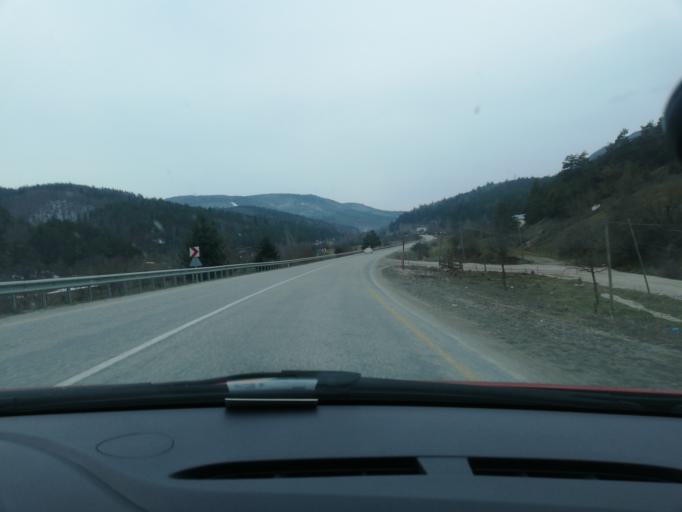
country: TR
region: Kastamonu
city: Kure
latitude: 41.7608
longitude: 33.7087
